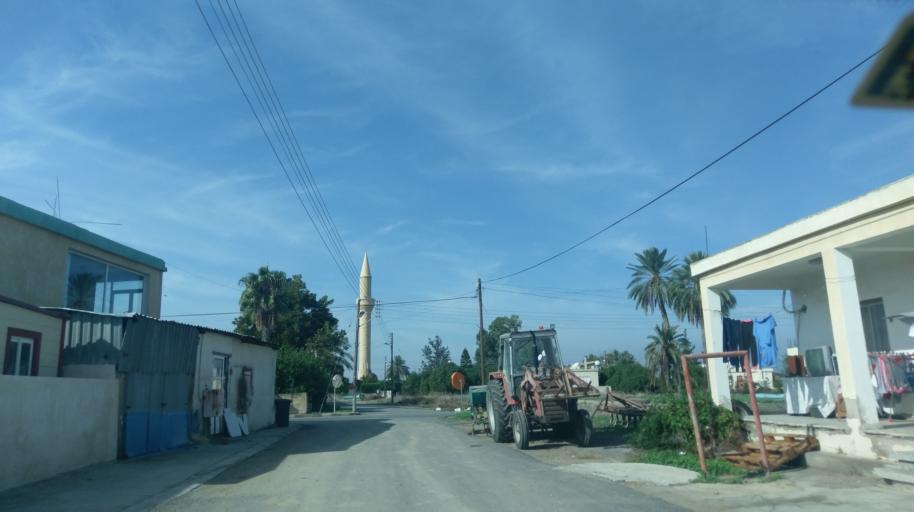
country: CY
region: Ammochostos
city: Lefkonoiko
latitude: 35.1675
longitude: 33.6405
